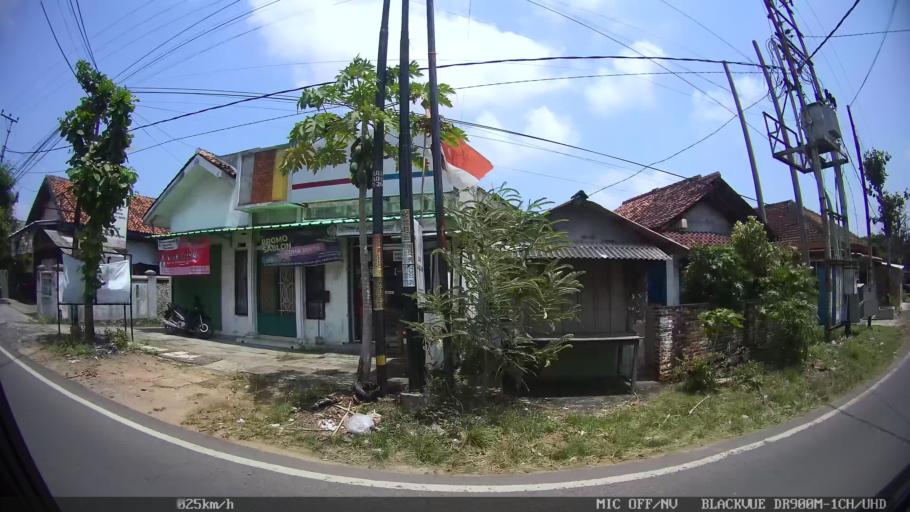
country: ID
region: Lampung
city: Kedaton
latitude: -5.3770
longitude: 105.2654
